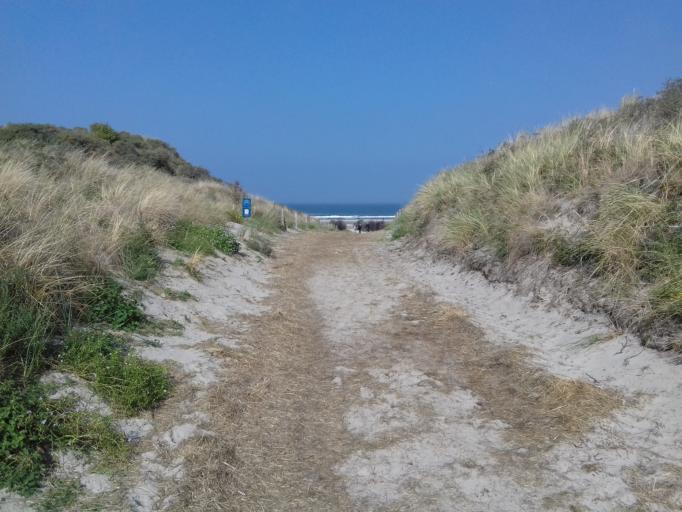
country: DE
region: Lower Saxony
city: Juist
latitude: 53.6821
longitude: 7.0251
